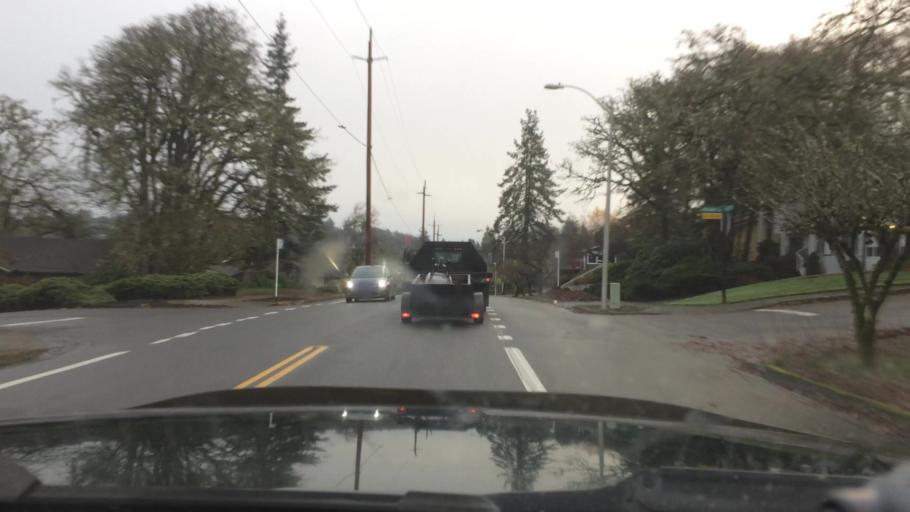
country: US
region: Oregon
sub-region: Lane County
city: Eugene
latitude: 44.0277
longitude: -123.1145
